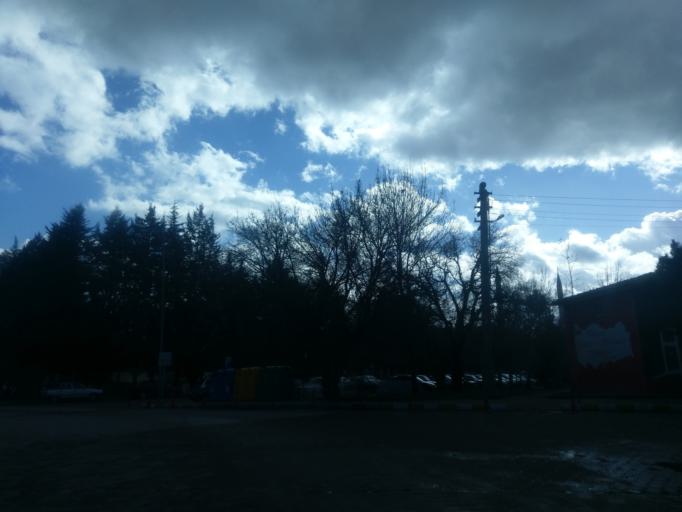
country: TR
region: Kuetahya
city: Gediz
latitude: 38.9913
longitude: 29.3948
